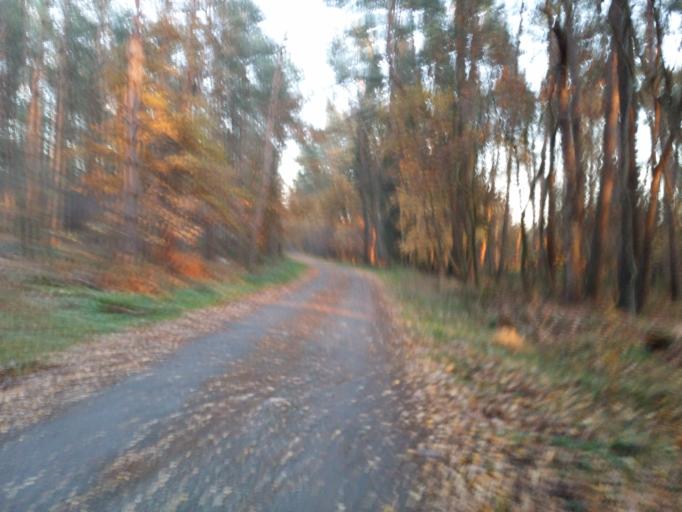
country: DE
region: Lower Saxony
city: Ahausen
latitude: 53.0923
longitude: 9.3096
